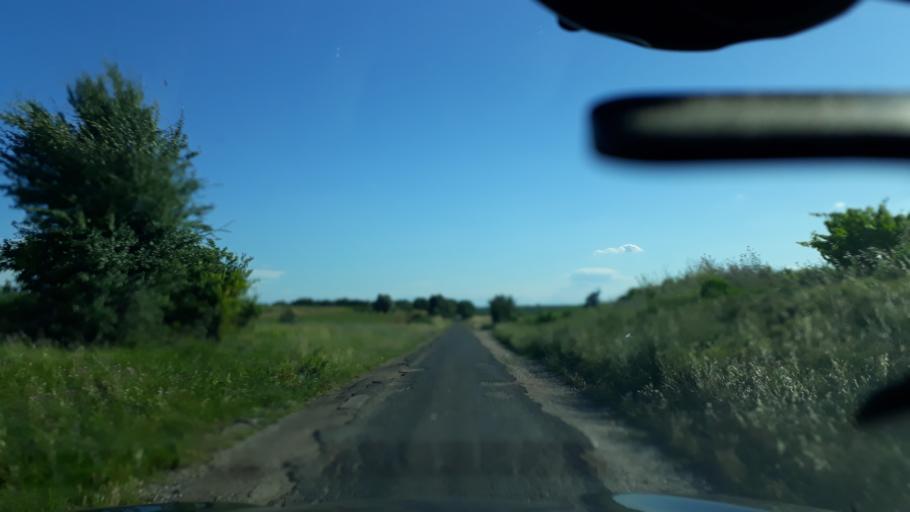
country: FR
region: Languedoc-Roussillon
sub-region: Departement de l'Herault
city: Marseillan
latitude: 43.3405
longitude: 3.5093
